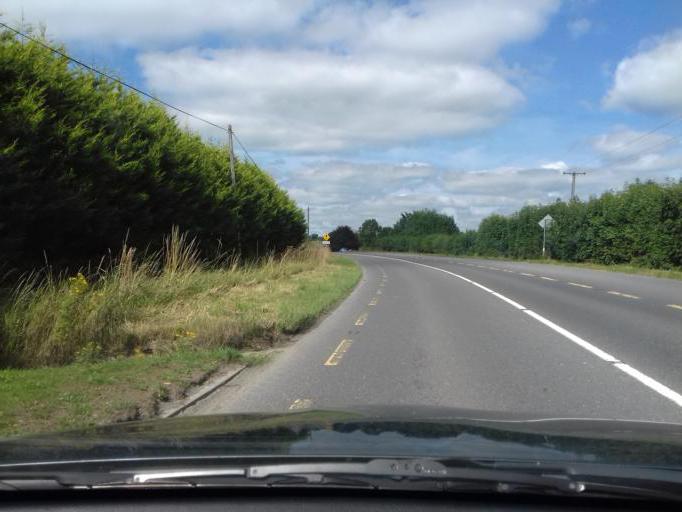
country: IE
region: Leinster
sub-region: Wicklow
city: Baltinglass
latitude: 53.0078
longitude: -6.6420
